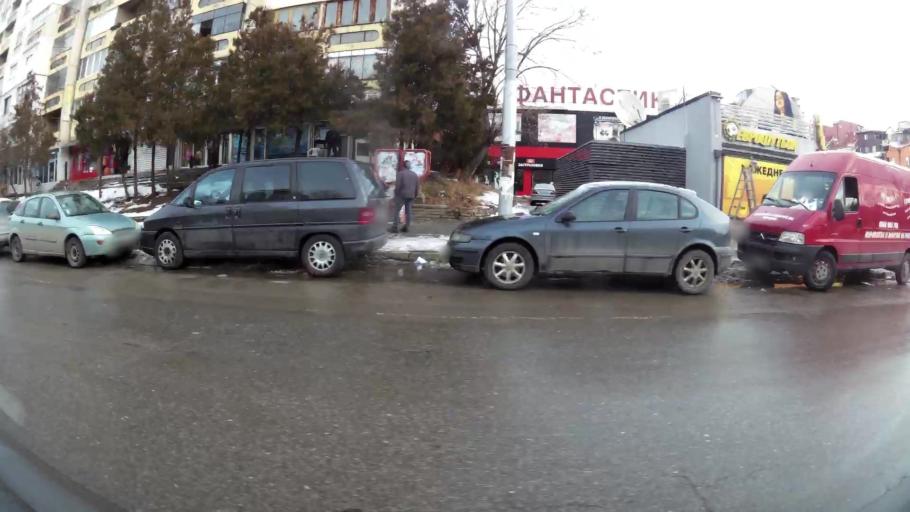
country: BG
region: Sofia-Capital
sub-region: Stolichna Obshtina
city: Sofia
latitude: 42.7073
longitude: 23.3507
